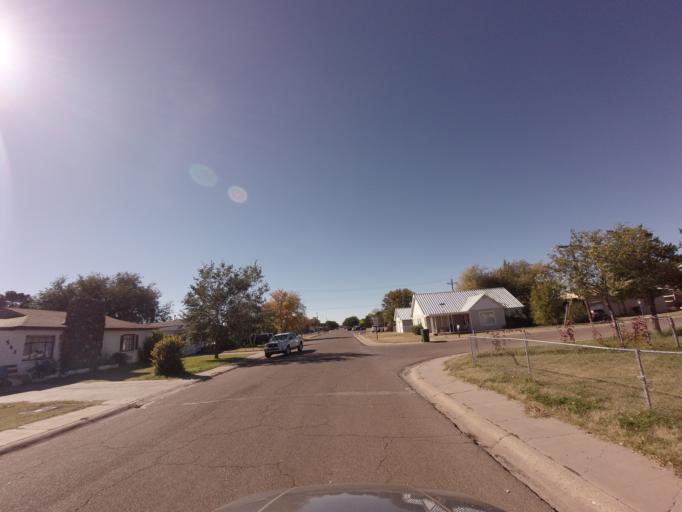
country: US
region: New Mexico
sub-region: Curry County
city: Clovis
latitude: 34.4255
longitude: -103.2046
